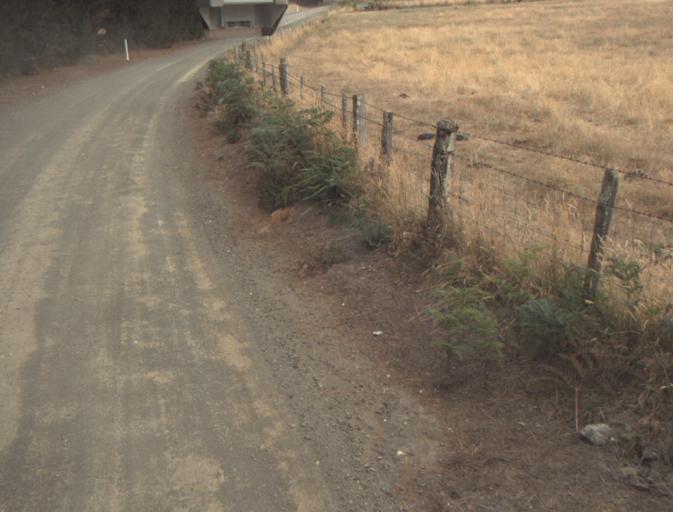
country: AU
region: Tasmania
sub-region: Launceston
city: Mayfield
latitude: -41.2106
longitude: 147.1842
